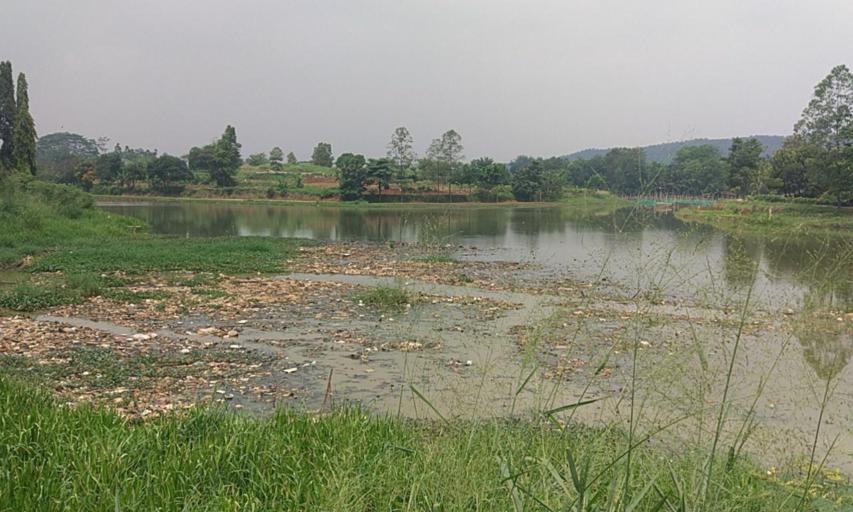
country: ID
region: West Java
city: Ciampea
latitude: -6.4951
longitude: 106.7453
